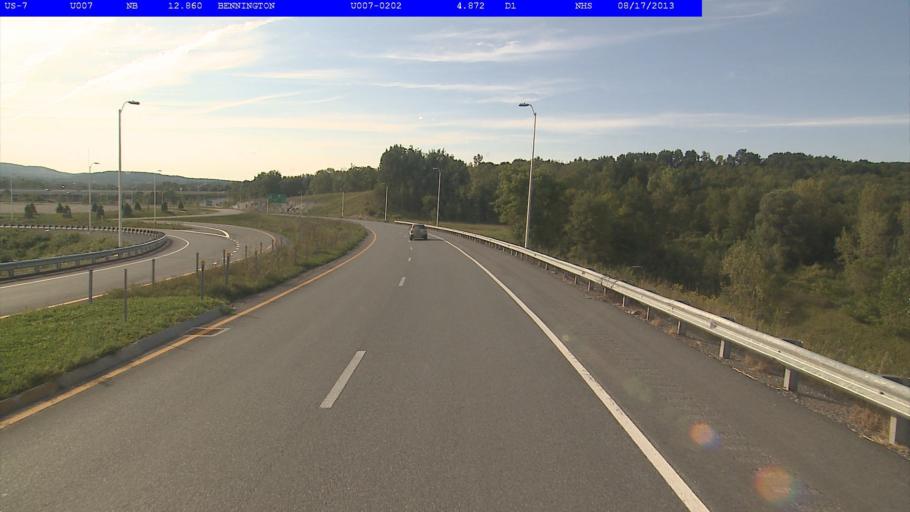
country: US
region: Vermont
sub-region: Bennington County
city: Bennington
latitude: 42.9044
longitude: -73.2007
